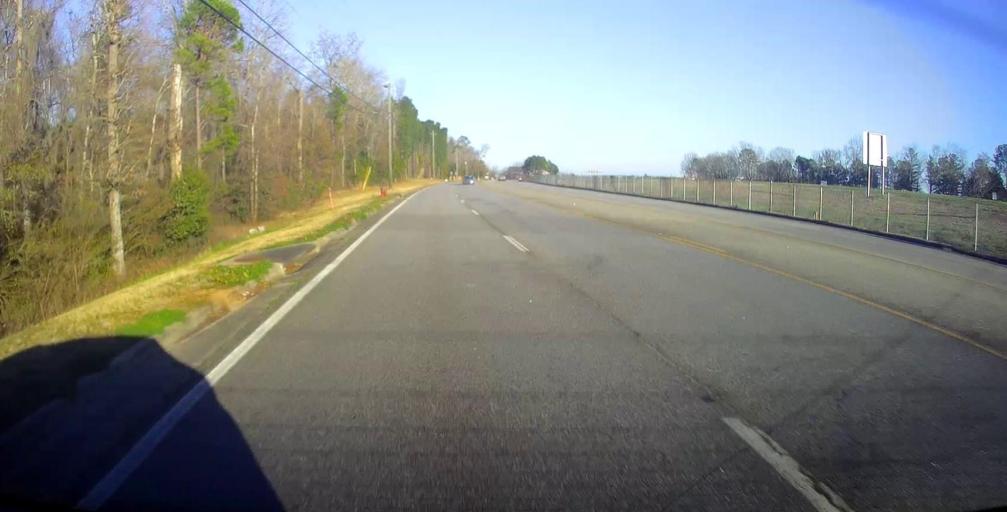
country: US
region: Georgia
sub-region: Dougherty County
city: Albany
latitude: 31.6235
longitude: -84.2245
